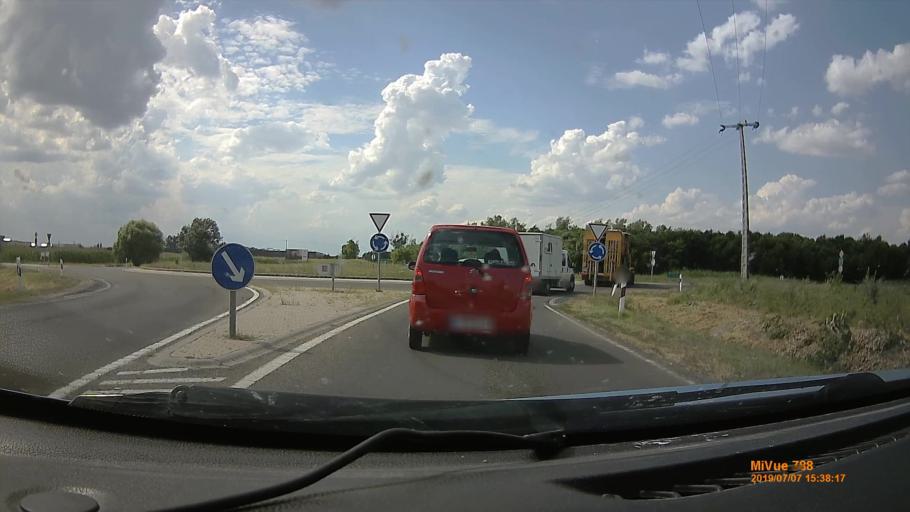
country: HU
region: Jasz-Nagykun-Szolnok
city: Jaszbereny
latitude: 47.4892
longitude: 19.9428
